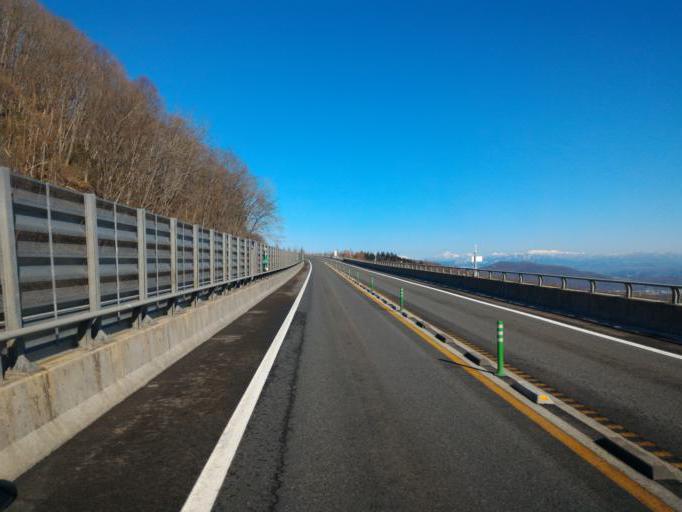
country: JP
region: Hokkaido
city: Otofuke
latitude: 43.0462
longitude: 142.7840
